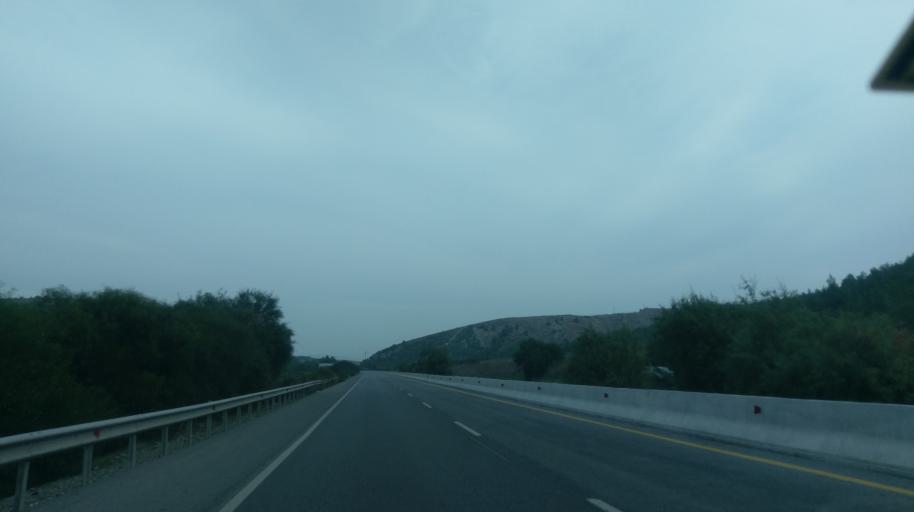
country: CY
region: Lefkosia
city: Akaki
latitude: 35.2067
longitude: 33.1197
